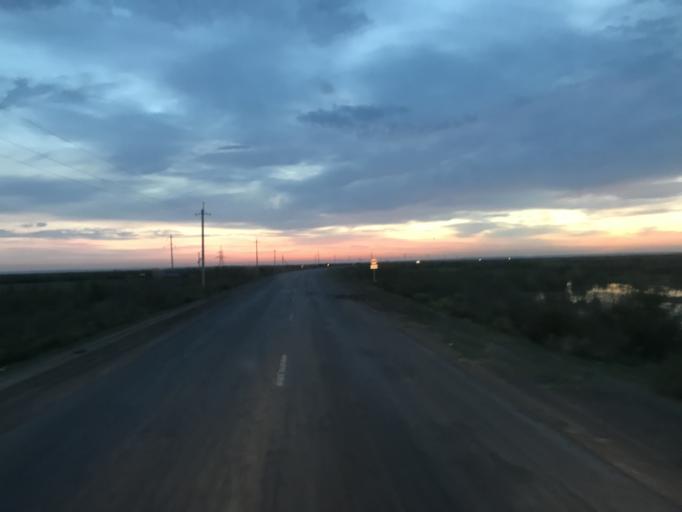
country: KZ
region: Ongtustik Qazaqstan
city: Asykata
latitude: 41.0017
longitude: 68.4700
